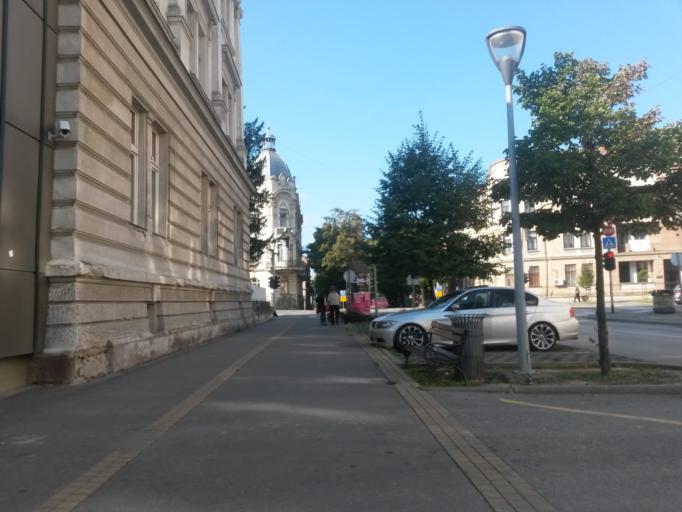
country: HR
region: Osjecko-Baranjska
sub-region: Grad Osijek
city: Osijek
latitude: 45.5599
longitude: 18.6856
